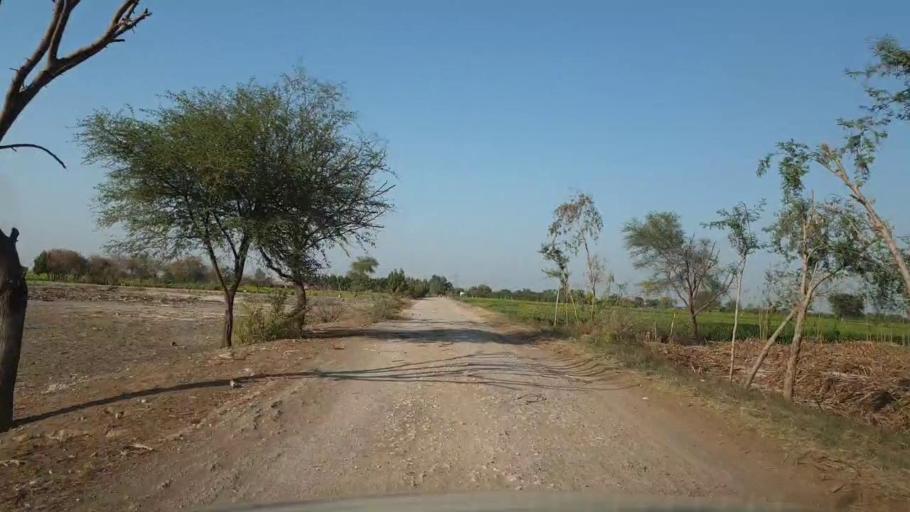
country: PK
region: Sindh
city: Tando Allahyar
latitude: 25.5085
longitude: 68.6551
